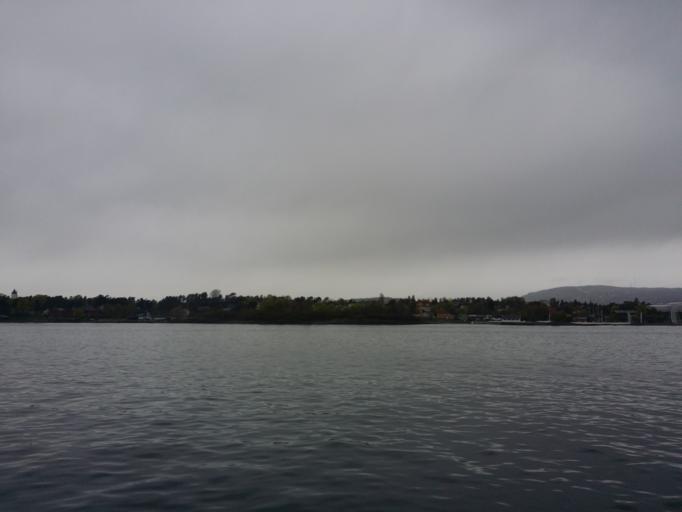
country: NO
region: Oslo
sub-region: Oslo
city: Sjolyststranda
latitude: 59.8939
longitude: 10.6966
